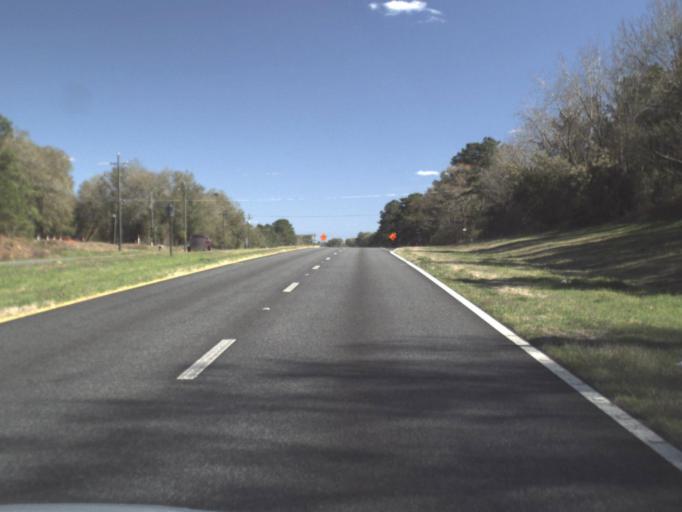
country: US
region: Florida
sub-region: Gadsden County
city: Quincy
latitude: 30.5634
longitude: -84.5404
